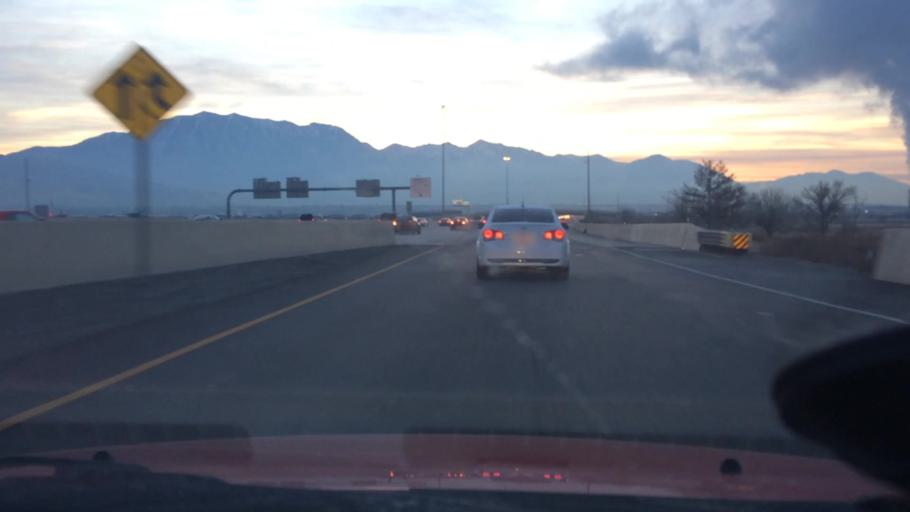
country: US
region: Utah
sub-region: Utah County
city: Pleasant Grove
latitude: 40.3478
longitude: -111.7664
